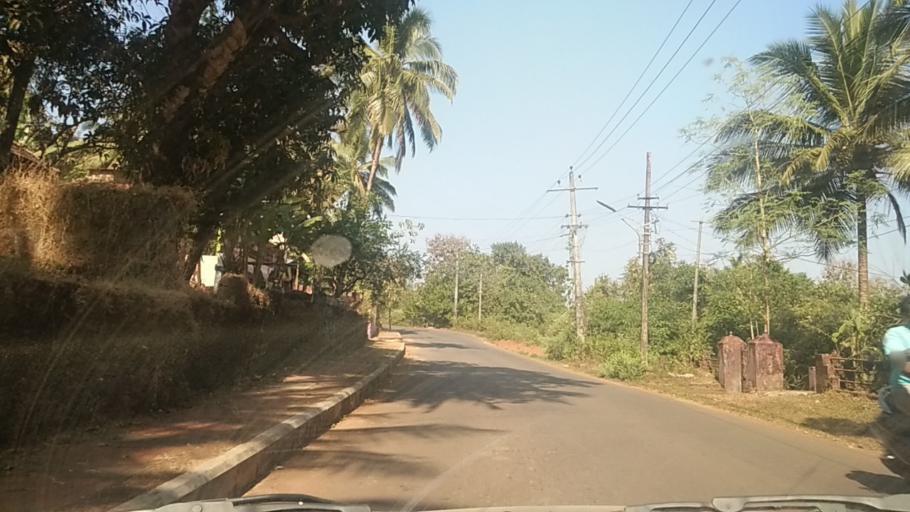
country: IN
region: Goa
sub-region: South Goa
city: Sanguem
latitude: 15.2256
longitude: 74.1596
